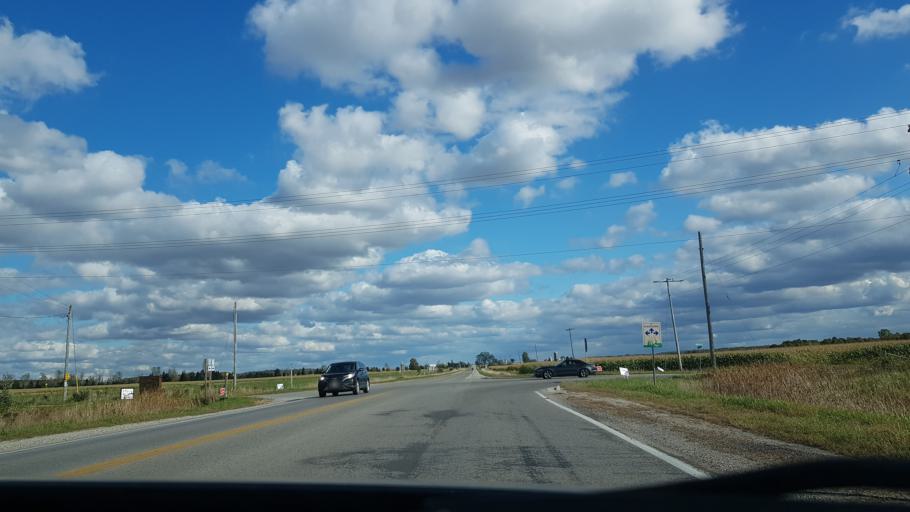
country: CA
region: Ontario
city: South Huron
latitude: 43.1493
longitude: -81.6630
